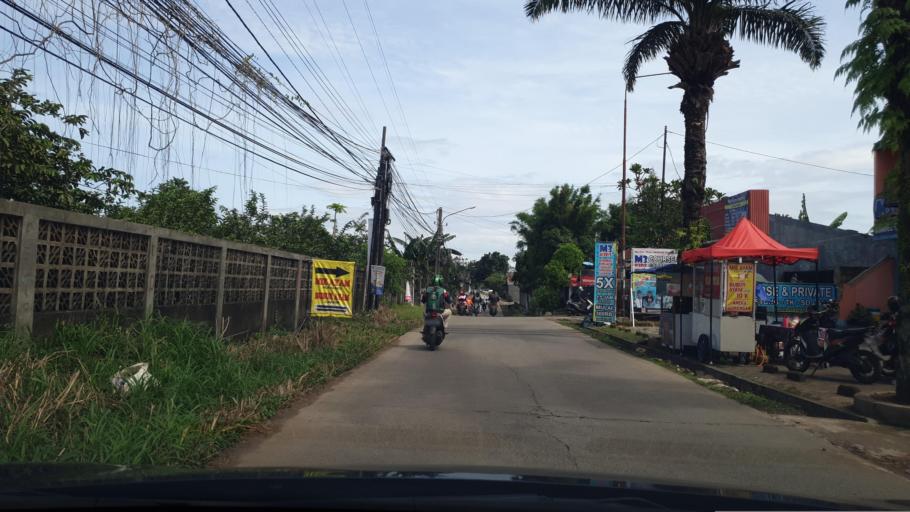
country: ID
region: West Java
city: Sawangan
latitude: -6.4083
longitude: 106.7702
